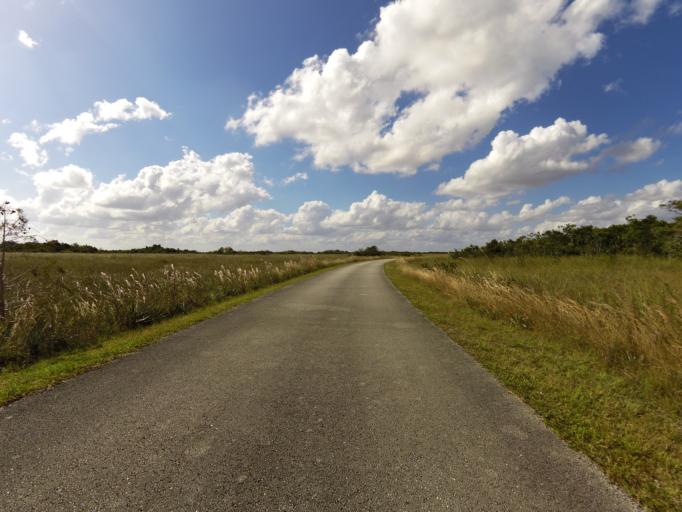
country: US
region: Florida
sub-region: Miami-Dade County
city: The Hammocks
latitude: 25.7176
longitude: -80.7610
